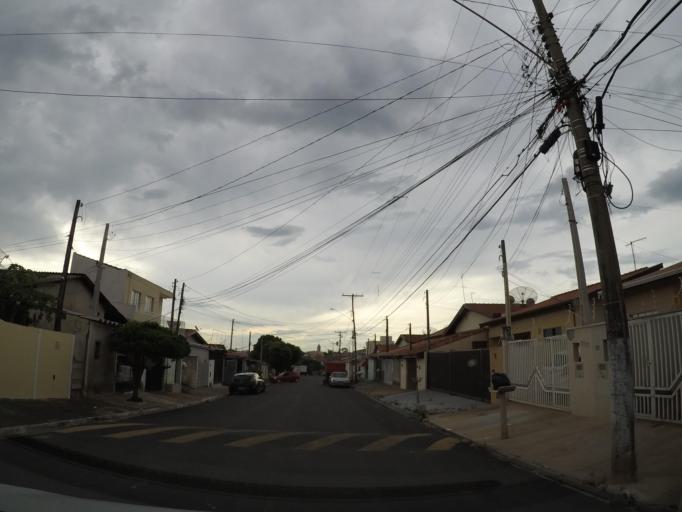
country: BR
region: Sao Paulo
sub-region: Sumare
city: Sumare
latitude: -22.8157
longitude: -47.2522
